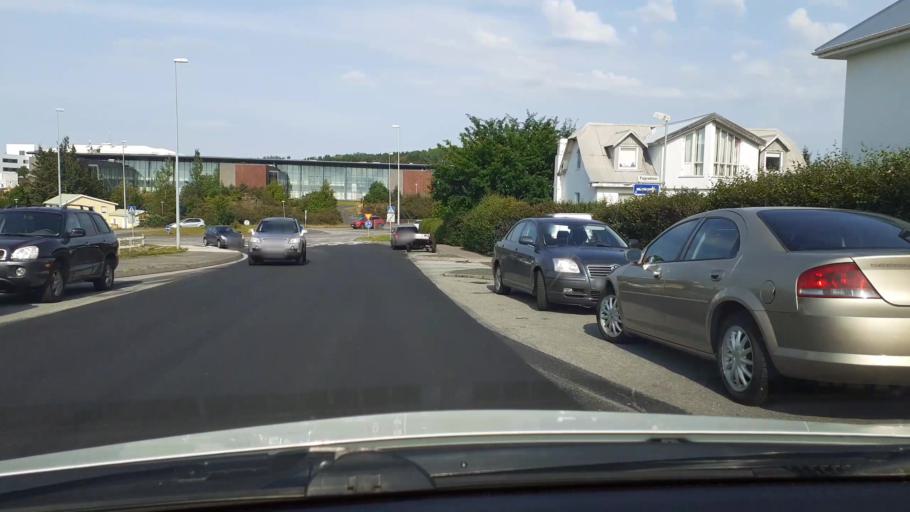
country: IS
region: Capital Region
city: Hafnarfjoerdur
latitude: 64.0664
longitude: -21.9440
